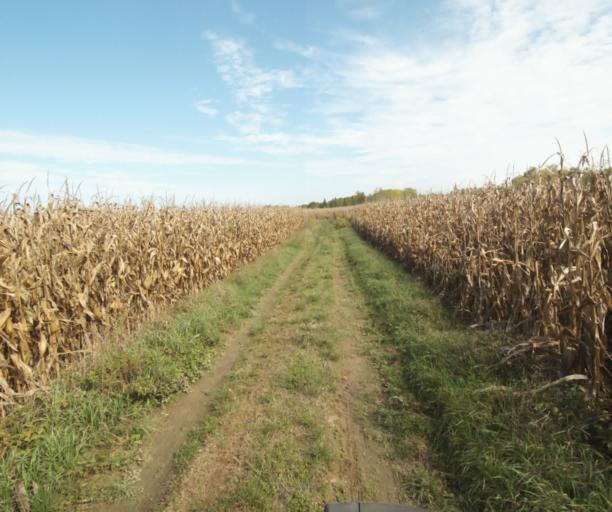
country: FR
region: Midi-Pyrenees
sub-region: Departement du Tarn-et-Garonne
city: Finhan
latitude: 43.9074
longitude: 1.2116
